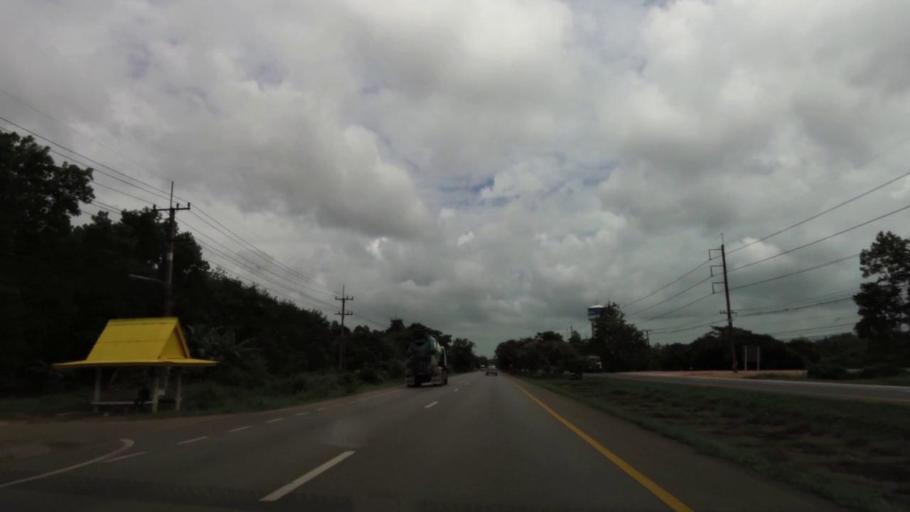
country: TH
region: Chanthaburi
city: Na Yai Am
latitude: 12.7471
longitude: 101.8792
